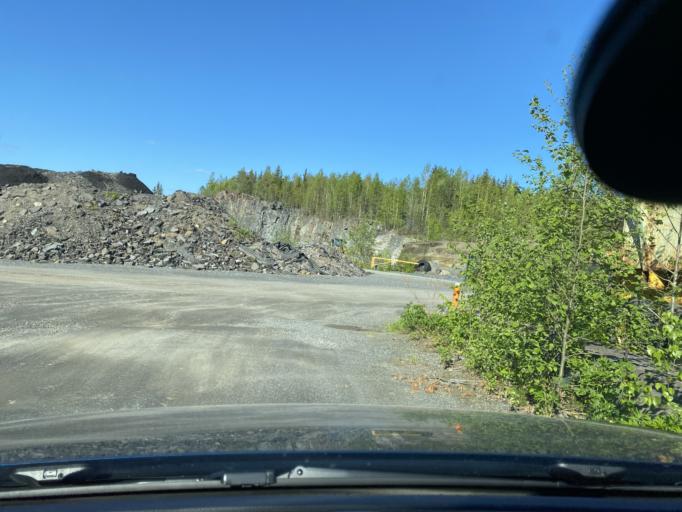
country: FI
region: Pirkanmaa
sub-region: Lounais-Pirkanmaa
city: Punkalaidun
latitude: 61.0760
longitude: 23.0798
